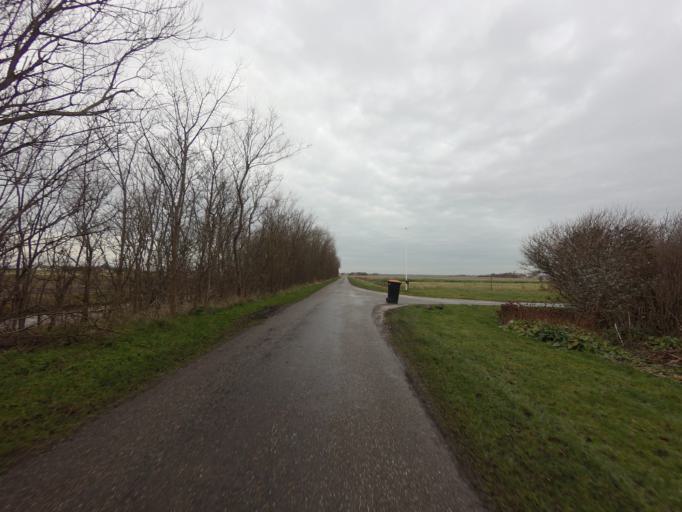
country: NL
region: North Holland
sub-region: Gemeente Texel
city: Den Burg
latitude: 53.0196
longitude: 4.8004
